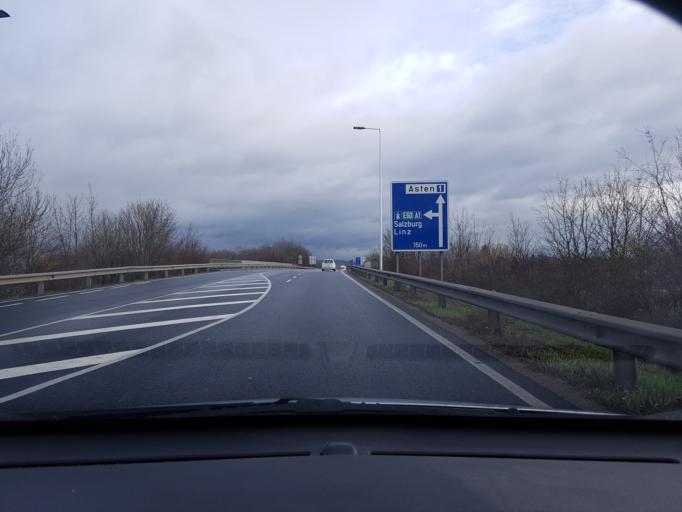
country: AT
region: Upper Austria
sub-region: Politischer Bezirk Linz-Land
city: Asten
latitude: 48.2175
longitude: 14.4068
